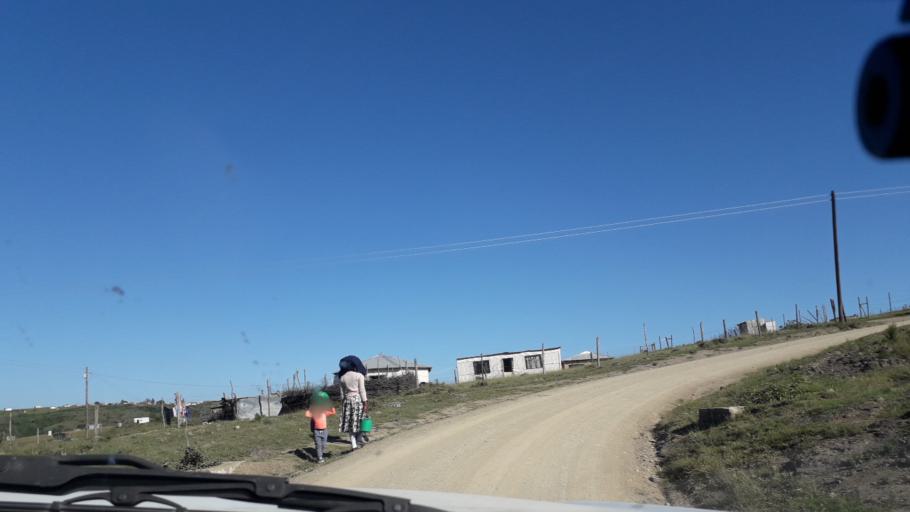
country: ZA
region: Eastern Cape
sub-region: Buffalo City Metropolitan Municipality
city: East London
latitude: -32.7999
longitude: 27.9668
